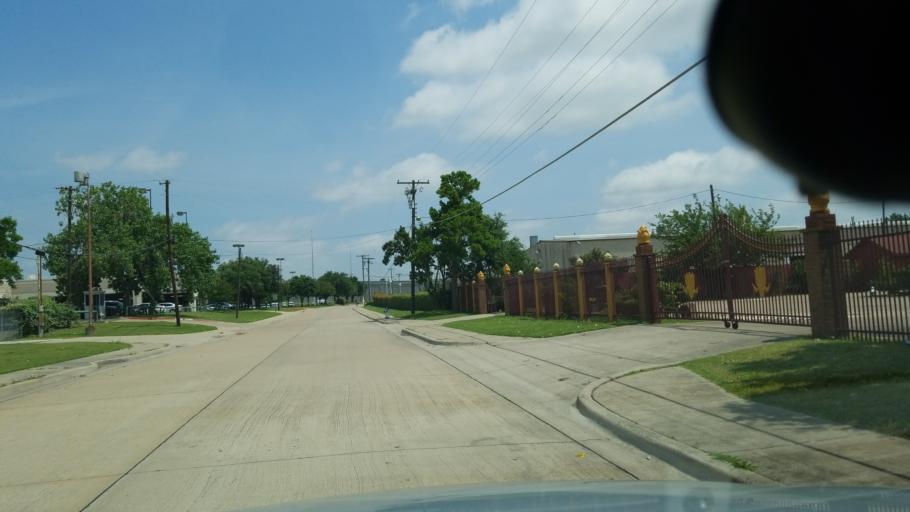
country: US
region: Texas
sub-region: Dallas County
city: Irving
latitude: 32.8341
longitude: -96.9380
